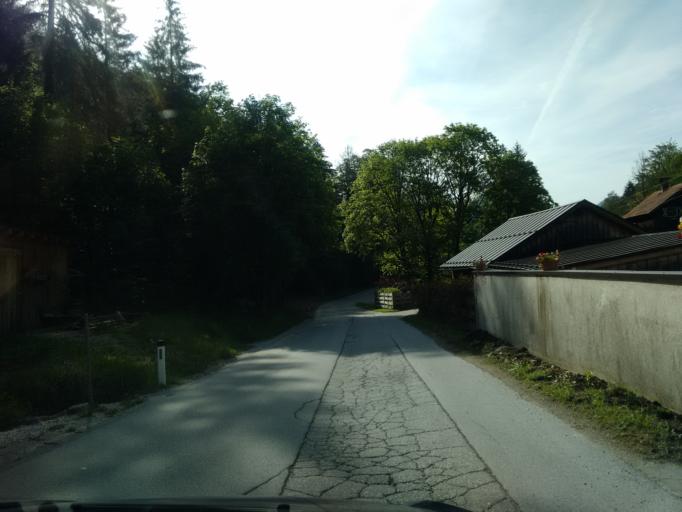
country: AT
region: Styria
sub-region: Politischer Bezirk Liezen
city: Altaussee
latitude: 47.6495
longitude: 13.7552
